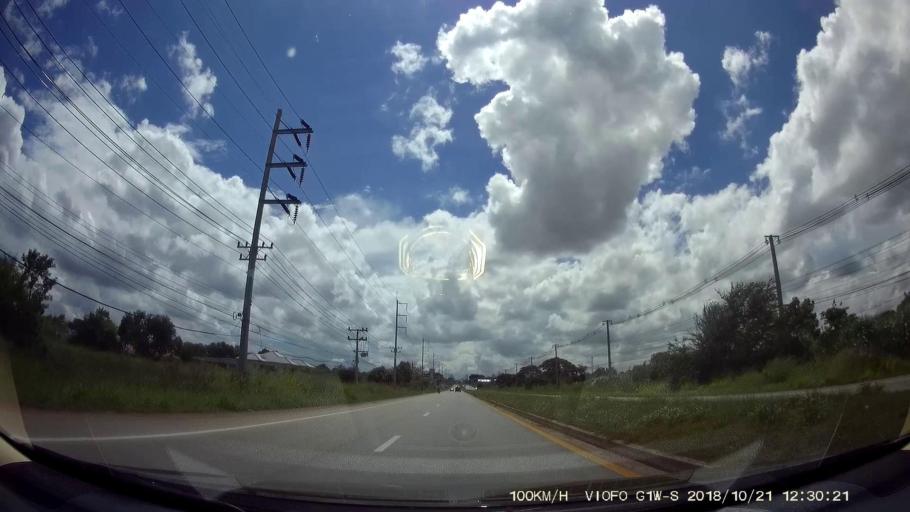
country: TH
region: Nakhon Ratchasima
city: Dan Khun Thot
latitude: 15.1722
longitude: 101.7396
